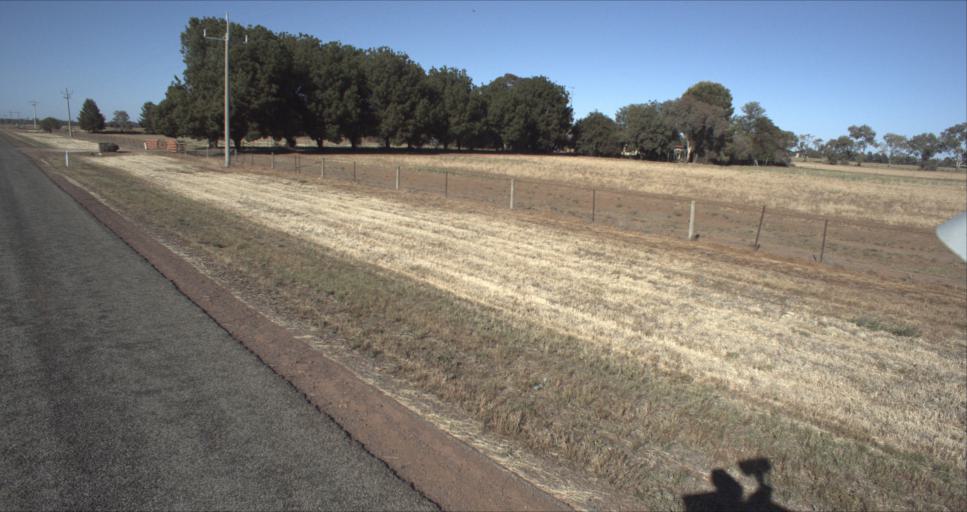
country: AU
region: New South Wales
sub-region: Leeton
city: Leeton
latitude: -34.5860
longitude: 146.2606
